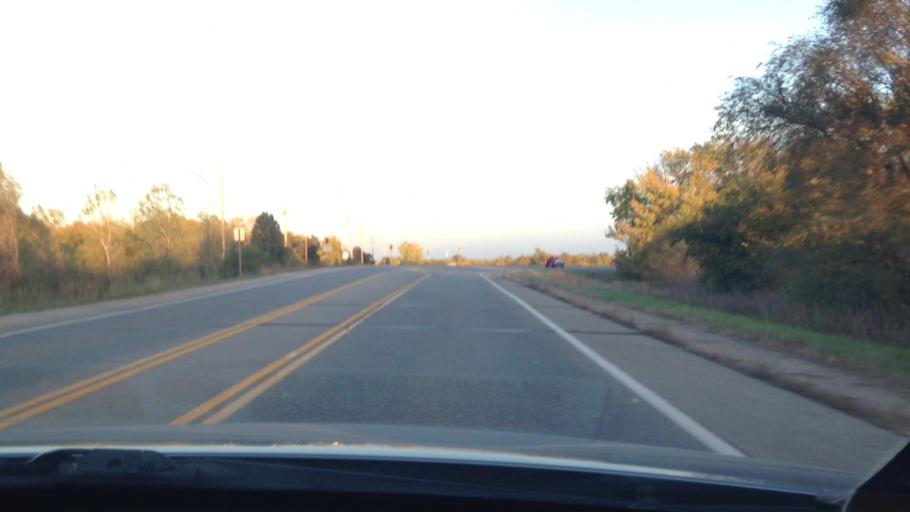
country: US
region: Kansas
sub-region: Johnson County
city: Olathe
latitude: 38.8545
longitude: -94.8732
